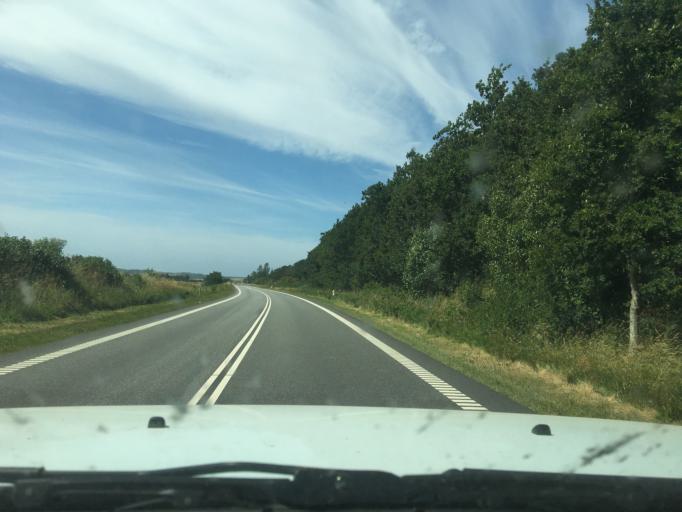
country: DK
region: Central Jutland
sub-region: Viborg Kommune
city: Viborg
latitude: 56.5471
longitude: 9.3993
